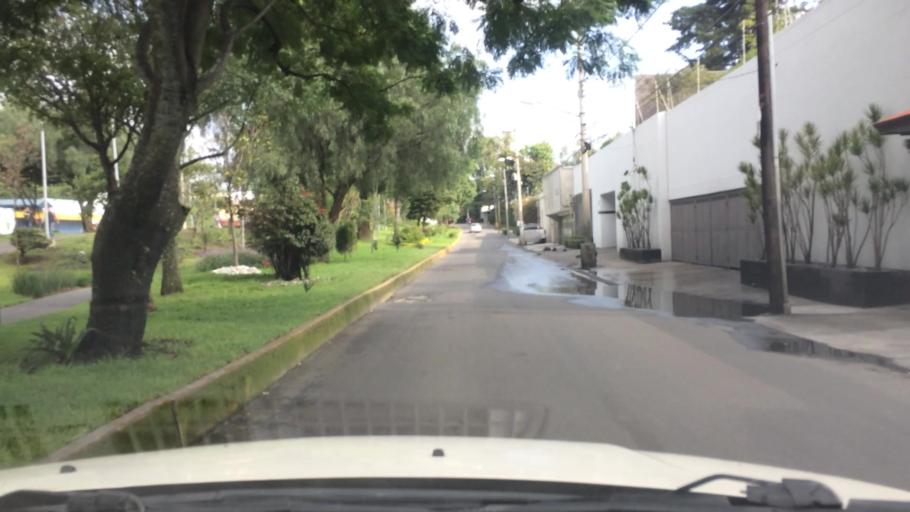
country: MX
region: Mexico City
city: Magdalena Contreras
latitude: 19.3175
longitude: -99.2137
